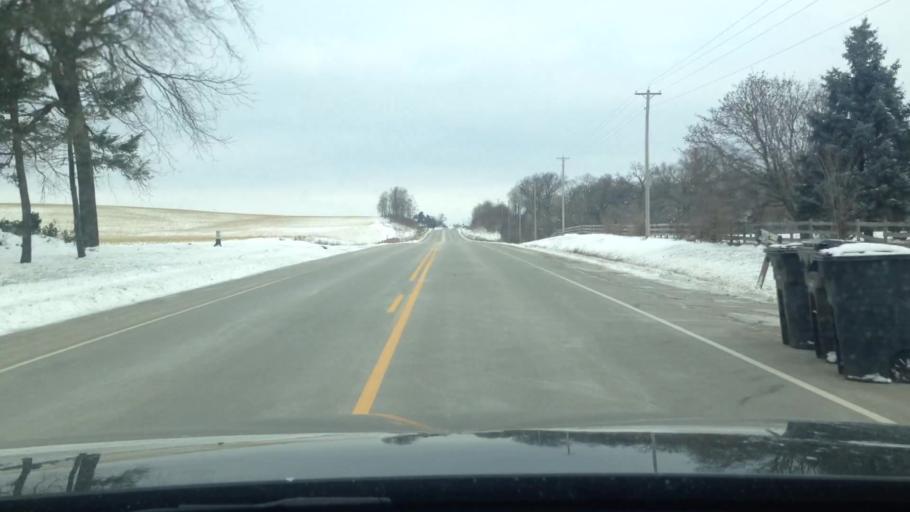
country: US
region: Wisconsin
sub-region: Walworth County
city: Lake Geneva
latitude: 42.5348
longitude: -88.4429
